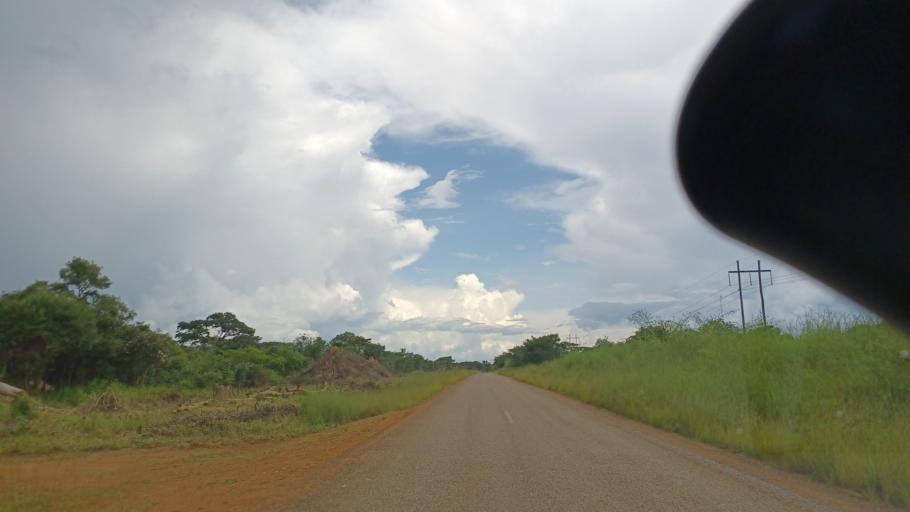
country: ZM
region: North-Western
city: Kasempa
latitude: -13.1257
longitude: 25.8724
